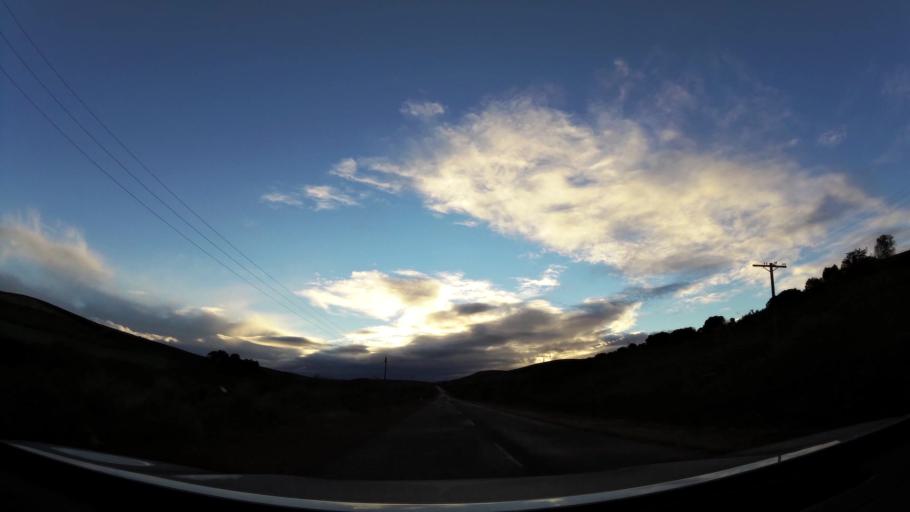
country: ZA
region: Western Cape
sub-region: Eden District Municipality
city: Riversdale
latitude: -34.0592
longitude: 20.8736
